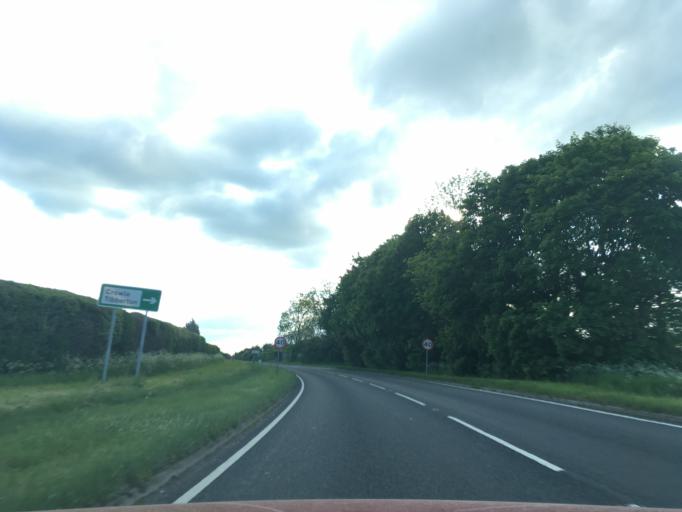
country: GB
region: England
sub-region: Worcestershire
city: Pershore
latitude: 52.1884
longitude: -2.1076
